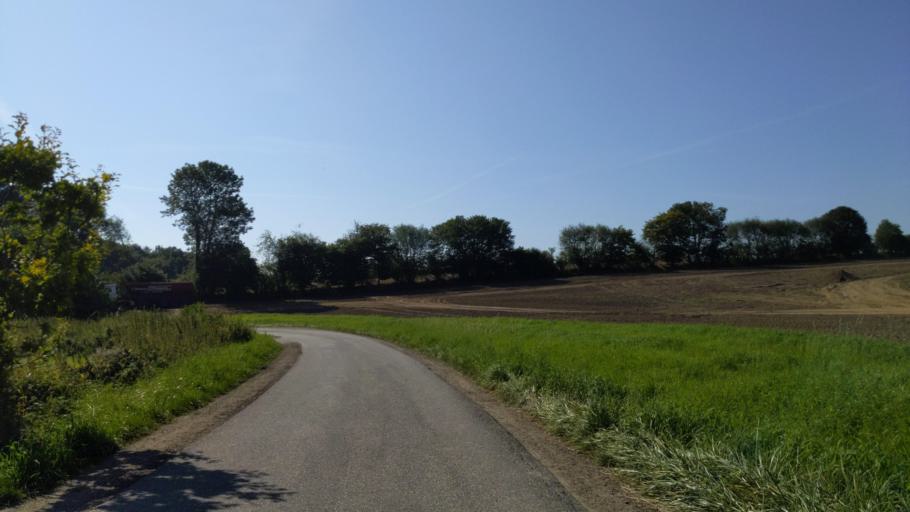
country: DE
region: Schleswig-Holstein
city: Heidekamp
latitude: 53.8460
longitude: 10.4884
